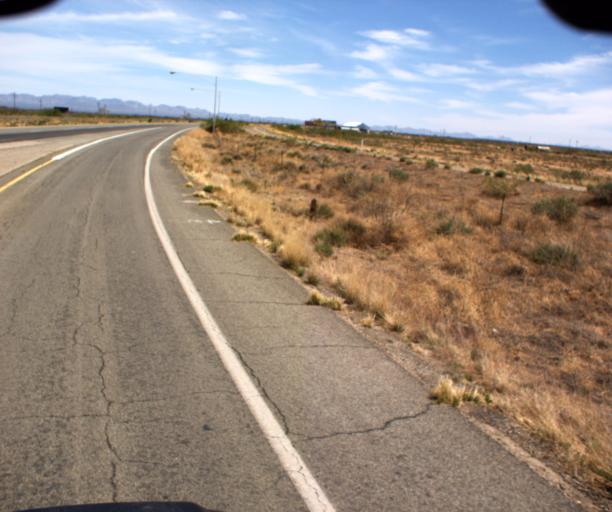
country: US
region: Arizona
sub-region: Cochise County
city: Willcox
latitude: 32.3171
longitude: -109.4444
